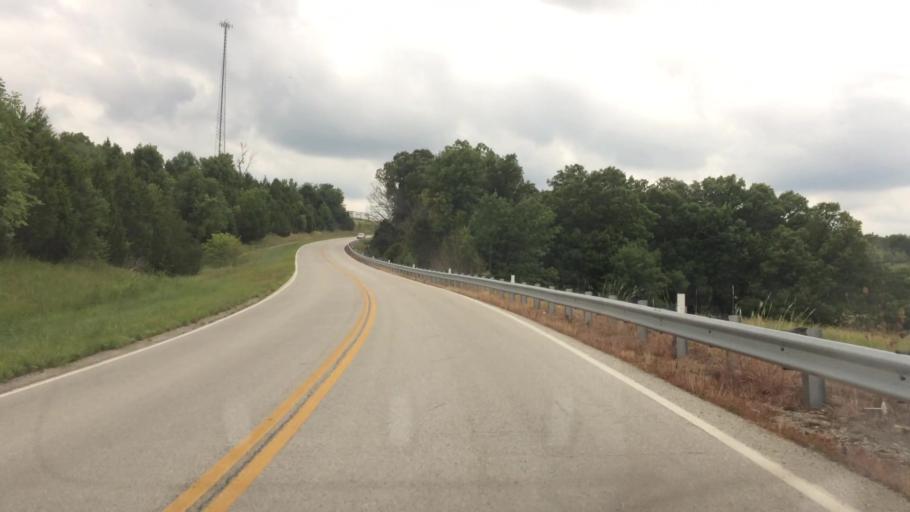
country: US
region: Missouri
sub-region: Webster County
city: Marshfield
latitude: 37.3033
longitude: -93.0073
